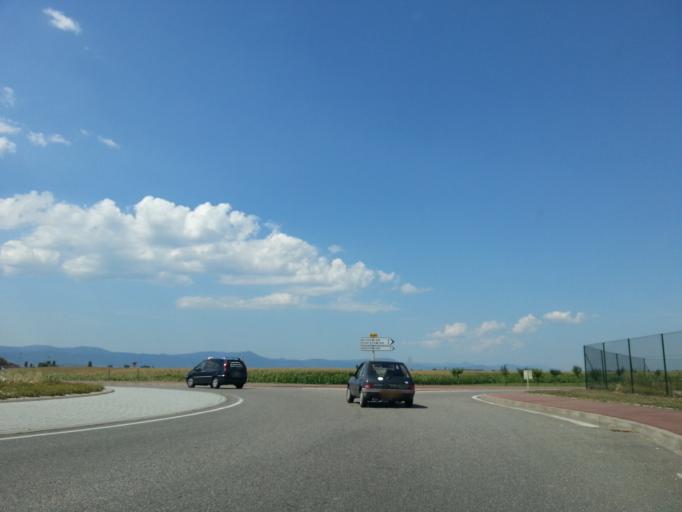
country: FR
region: Alsace
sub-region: Departement du Haut-Rhin
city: Andolsheim
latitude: 48.0663
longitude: 7.4178
